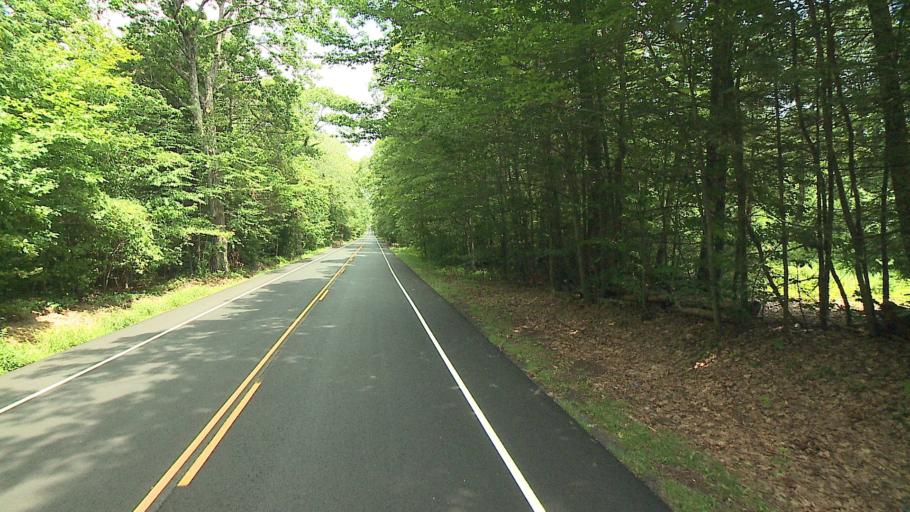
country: US
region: Connecticut
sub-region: Hartford County
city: North Granby
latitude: 42.0044
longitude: -72.8957
